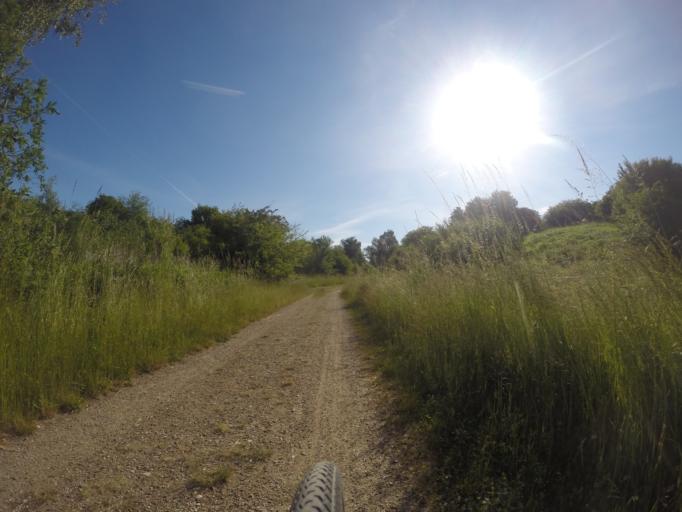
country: DK
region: Capital Region
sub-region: Ballerup Kommune
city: Ballerup
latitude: 55.7008
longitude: 12.3429
